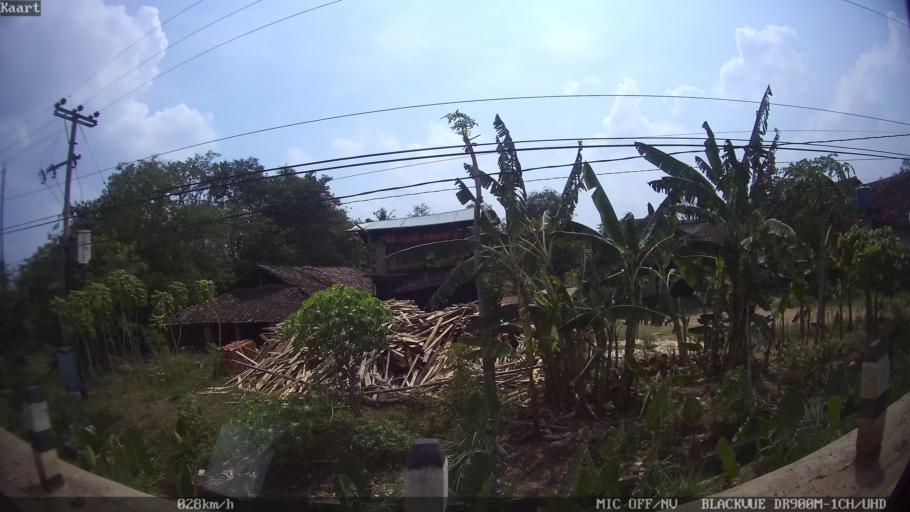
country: ID
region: Lampung
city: Pringsewu
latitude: -5.3798
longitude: 104.9682
